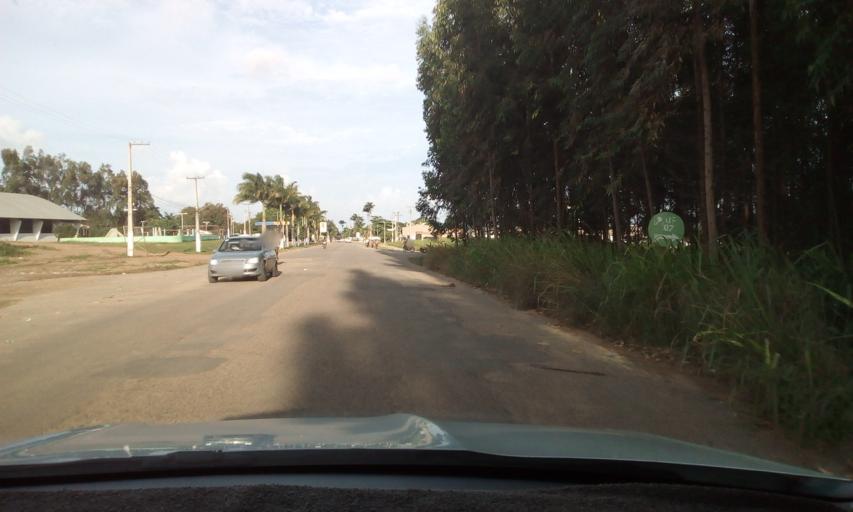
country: BR
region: Pernambuco
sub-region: Gloria Do Goita
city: Gloria do Goita
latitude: -7.9981
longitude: -35.2213
